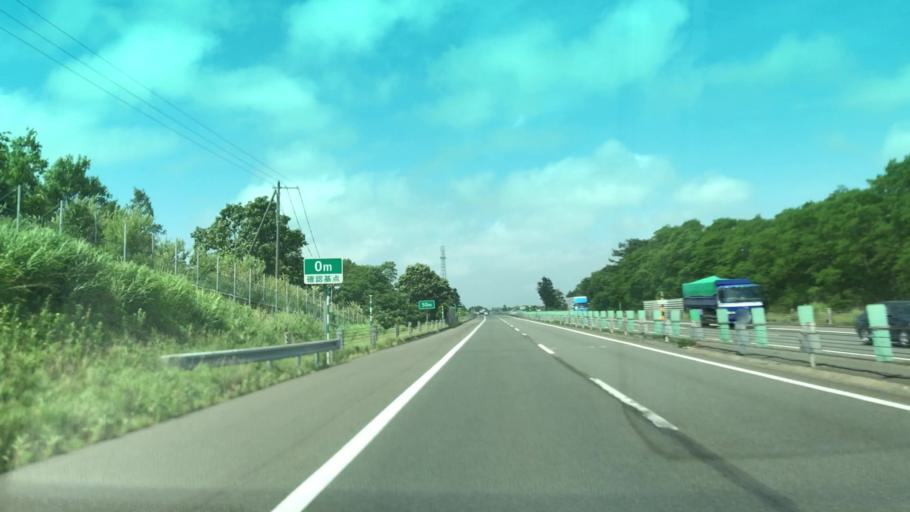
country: JP
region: Hokkaido
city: Kitahiroshima
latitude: 42.8956
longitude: 141.5498
